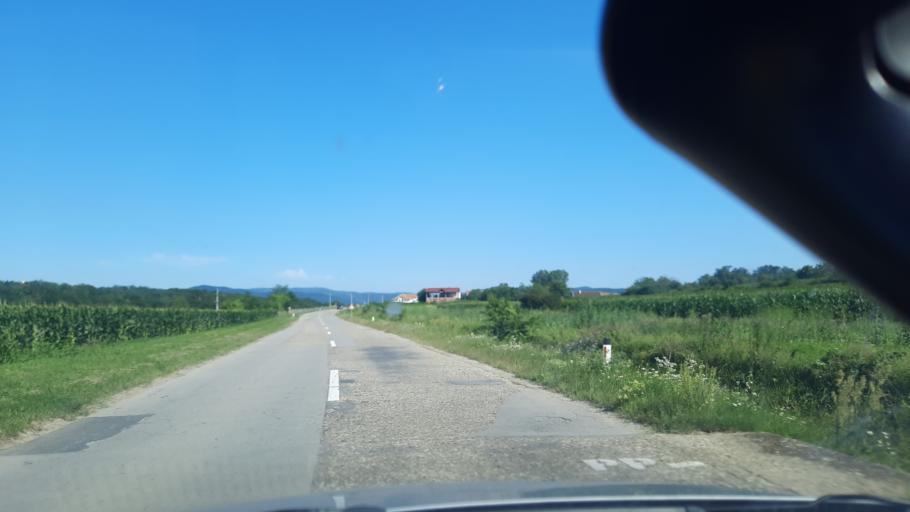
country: RS
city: Turija
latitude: 44.5567
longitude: 21.5408
